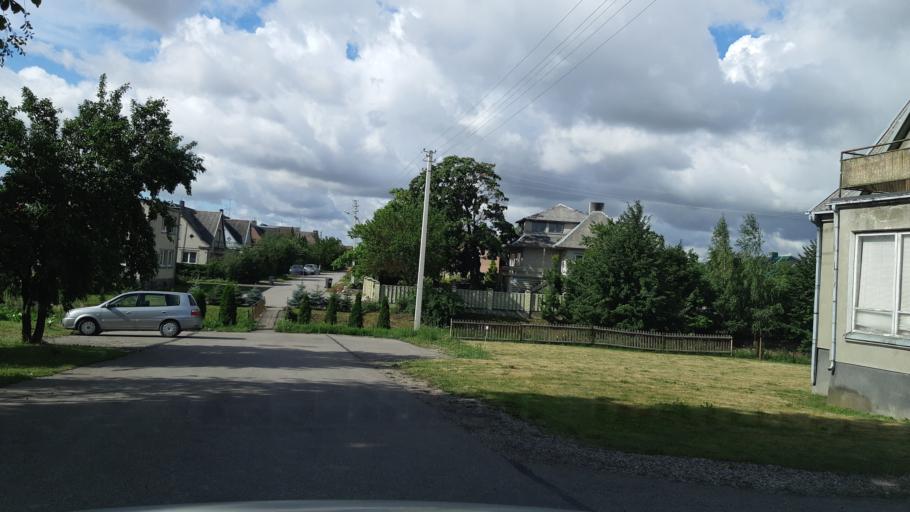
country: LT
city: Vilkaviskis
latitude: 54.6391
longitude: 23.0524
